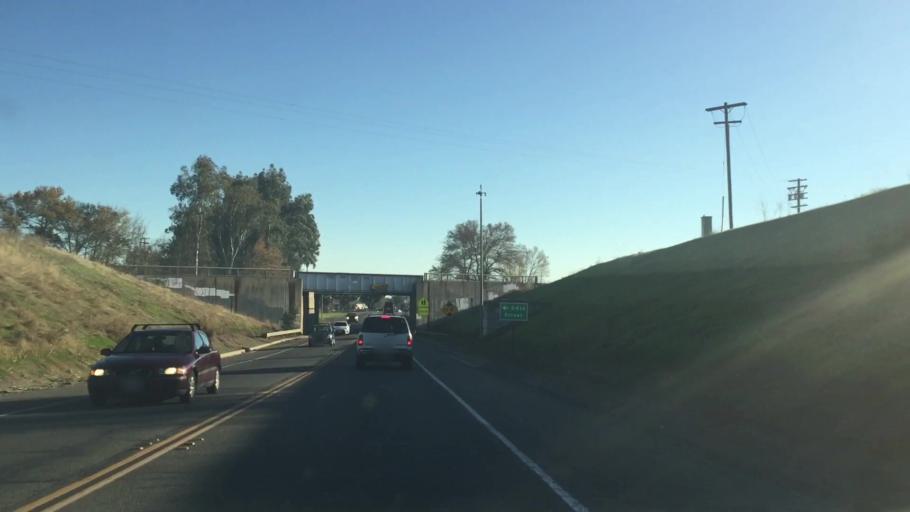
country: US
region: California
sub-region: Yuba County
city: Marysville
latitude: 39.1594
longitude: -121.5899
